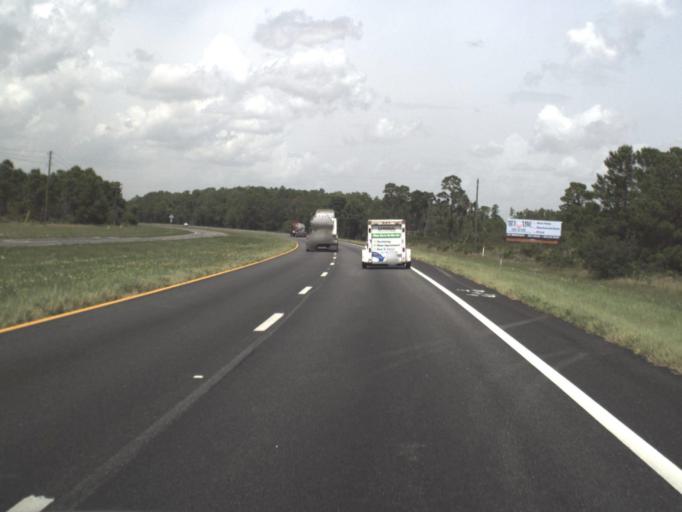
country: US
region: Florida
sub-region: Polk County
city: Frostproof
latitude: 27.7144
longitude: -81.5607
